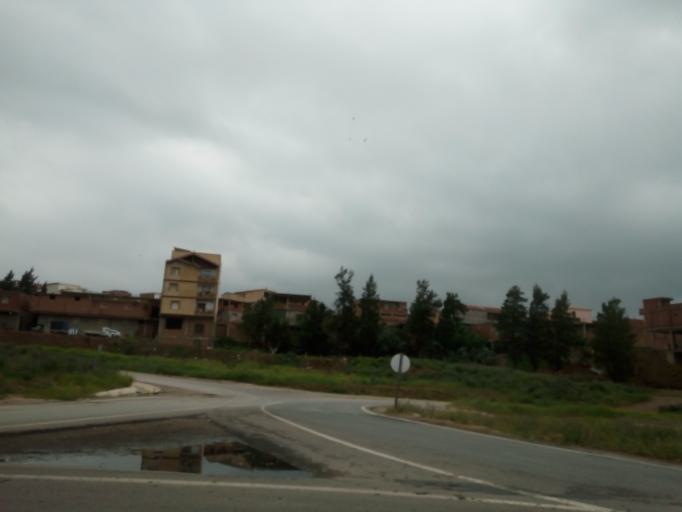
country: DZ
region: Blida
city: Chiffa
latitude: 36.4366
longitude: 2.7512
